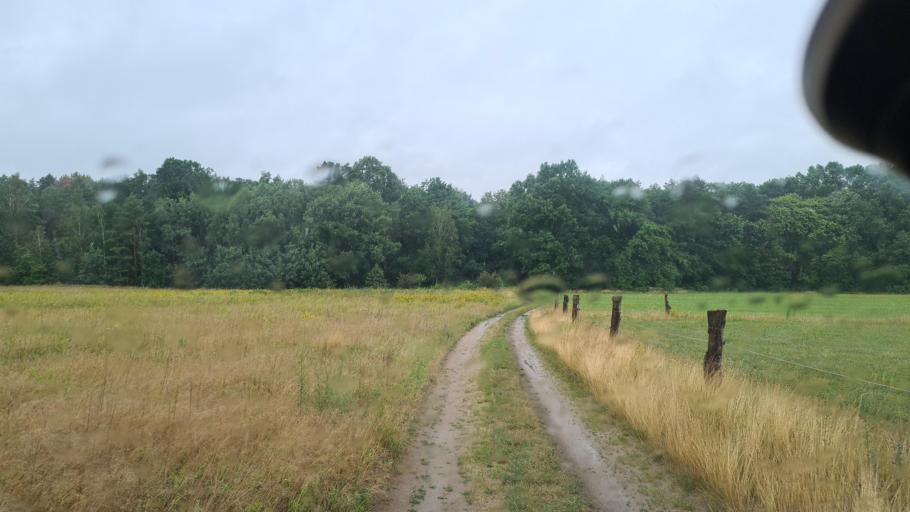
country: DE
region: Brandenburg
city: Juterbog
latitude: 51.9886
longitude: 13.1687
